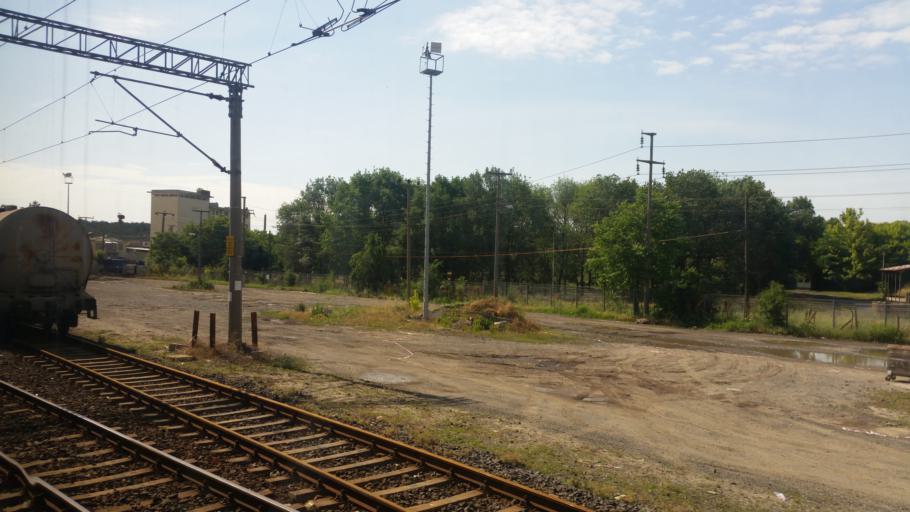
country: TR
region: Tekirdag
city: Corlu
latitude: 41.1779
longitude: 27.7770
